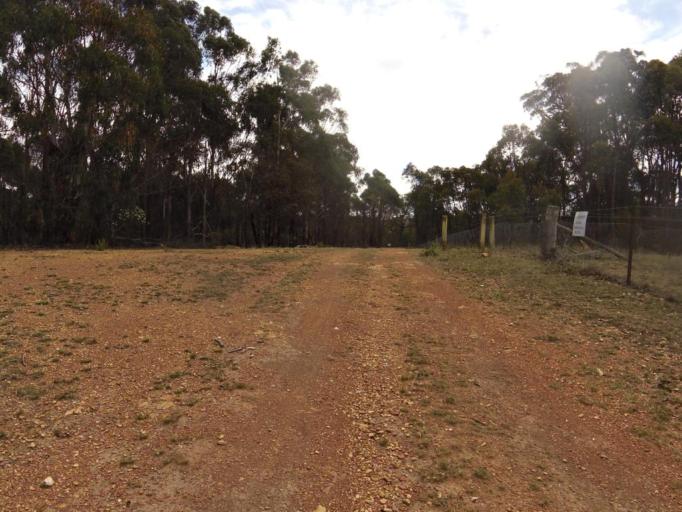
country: AU
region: Australian Capital Territory
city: Kaleen
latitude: -35.1278
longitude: 149.1308
